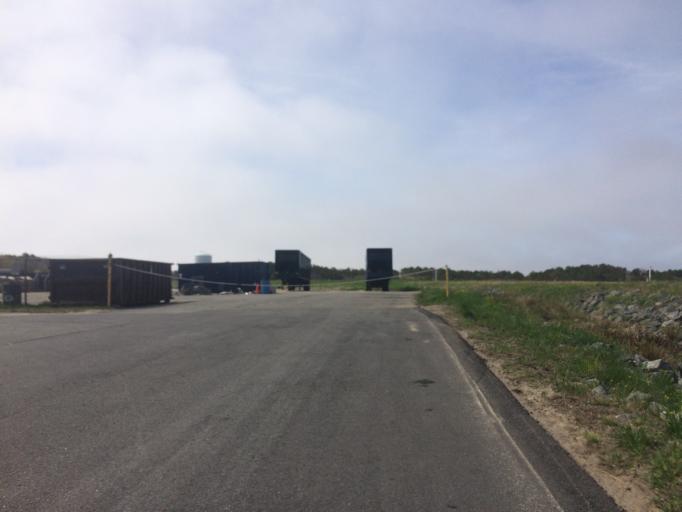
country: US
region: Massachusetts
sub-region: Barnstable County
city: Provincetown
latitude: 42.0603
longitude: -70.1951
